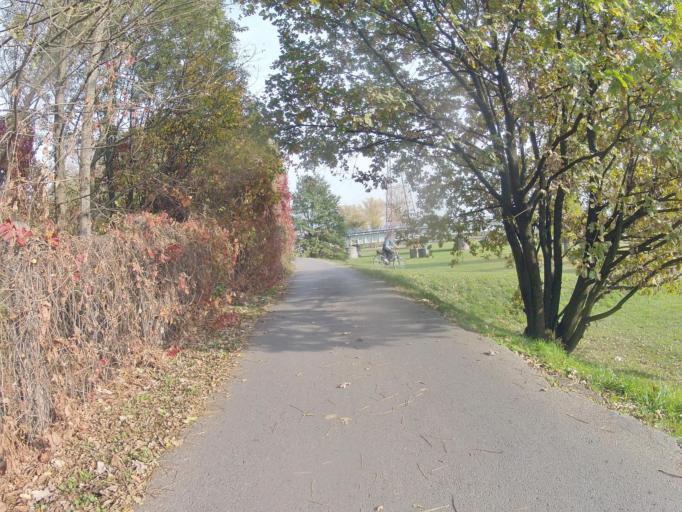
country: PL
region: Lesser Poland Voivodeship
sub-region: Krakow
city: Krakow
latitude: 50.0537
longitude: 19.9682
